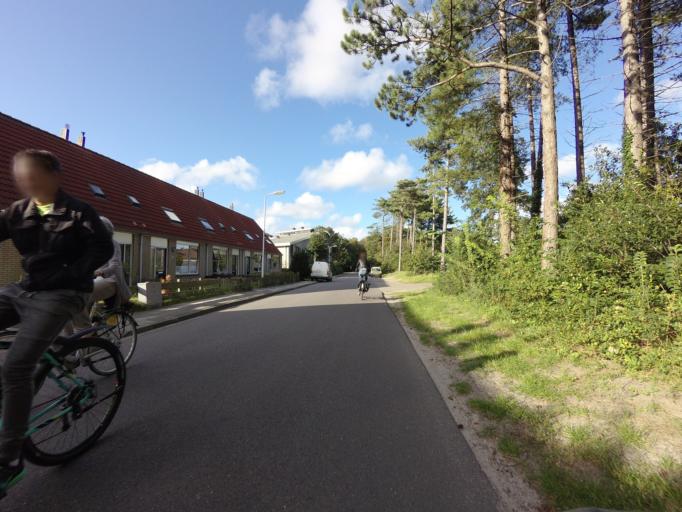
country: NL
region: Friesland
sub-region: Gemeente Terschelling
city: West-Terschelling
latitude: 53.3678
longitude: 5.2162
